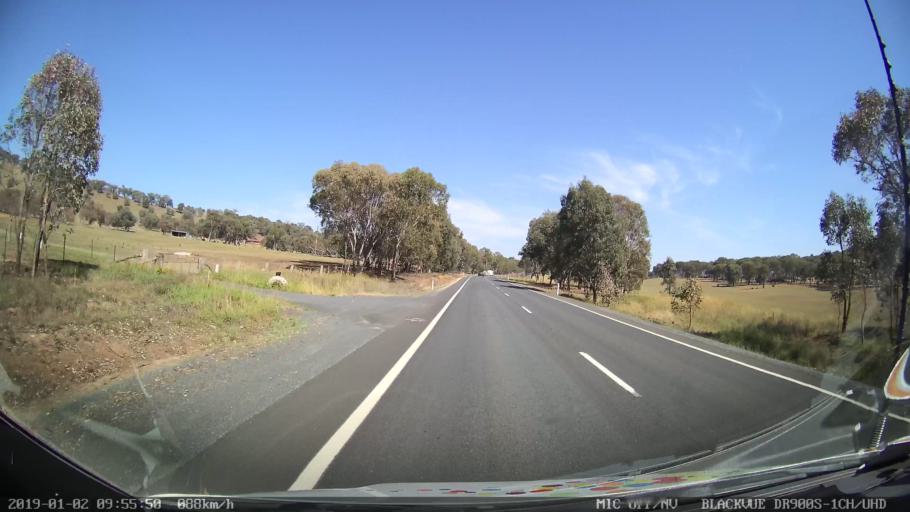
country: AU
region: New South Wales
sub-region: Tumut Shire
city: Tumut
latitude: -35.2205
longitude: 148.1833
